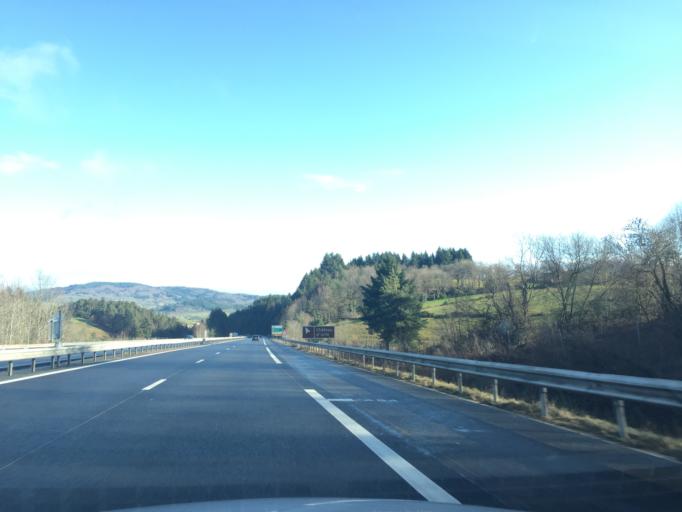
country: FR
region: Rhone-Alpes
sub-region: Departement de la Loire
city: Noiretable
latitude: 45.8511
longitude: 3.7712
